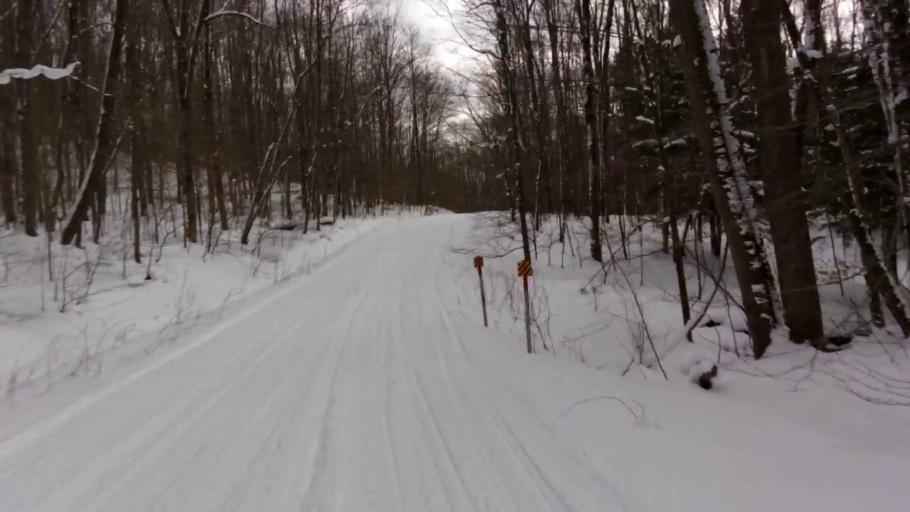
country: US
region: New York
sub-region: Cattaraugus County
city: Salamanca
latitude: 42.0519
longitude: -78.7532
